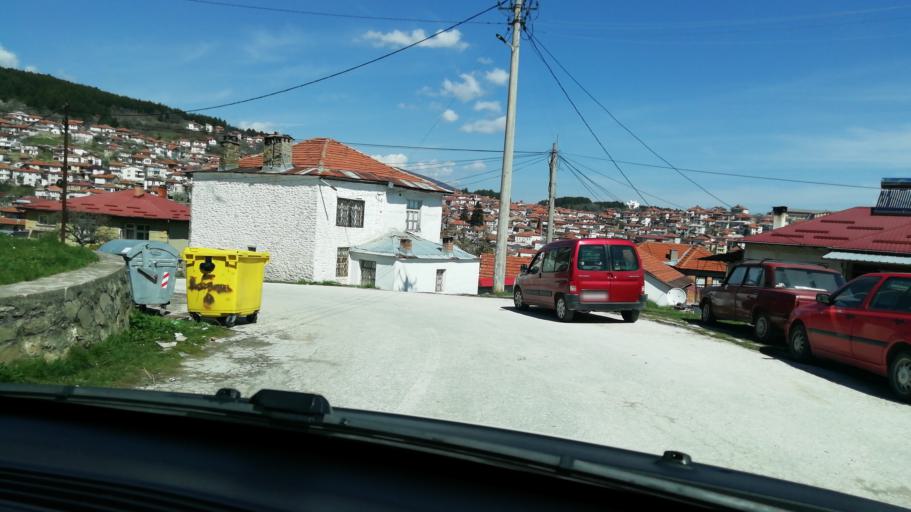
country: MK
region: Krusevo
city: Krushevo
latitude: 41.3653
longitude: 21.2501
